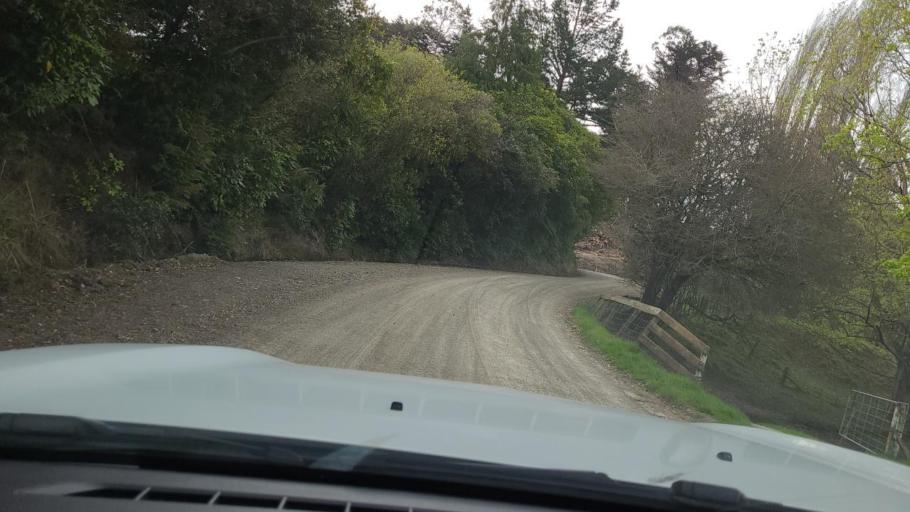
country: NZ
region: Hawke's Bay
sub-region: Napier City
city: Napier
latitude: -39.2889
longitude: 176.8411
